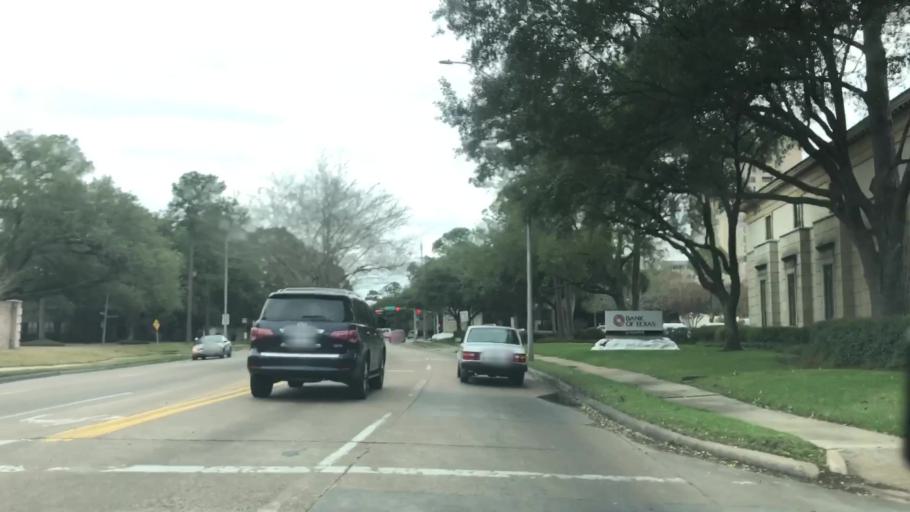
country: US
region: Texas
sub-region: Harris County
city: Hunters Creek Village
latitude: 29.7651
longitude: -95.4783
